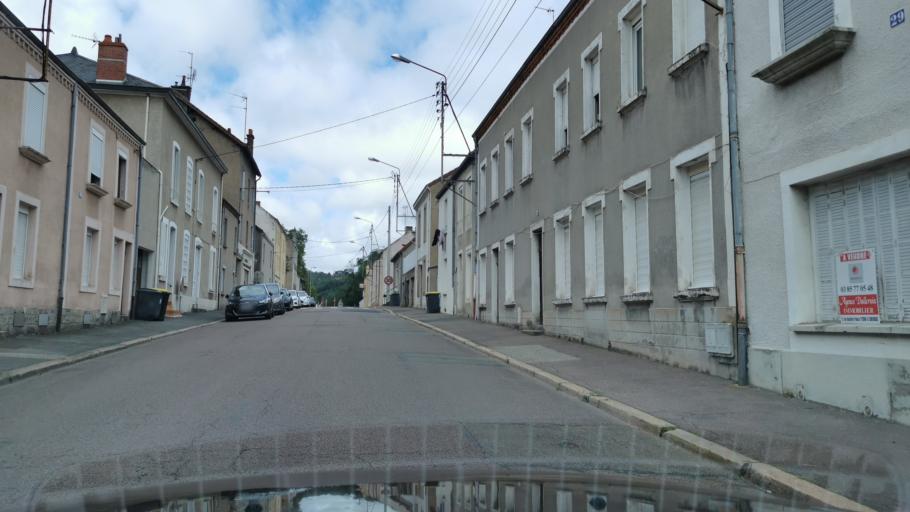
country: FR
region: Bourgogne
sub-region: Departement de Saone-et-Loire
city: Le Creusot
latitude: 46.8067
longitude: 4.4363
